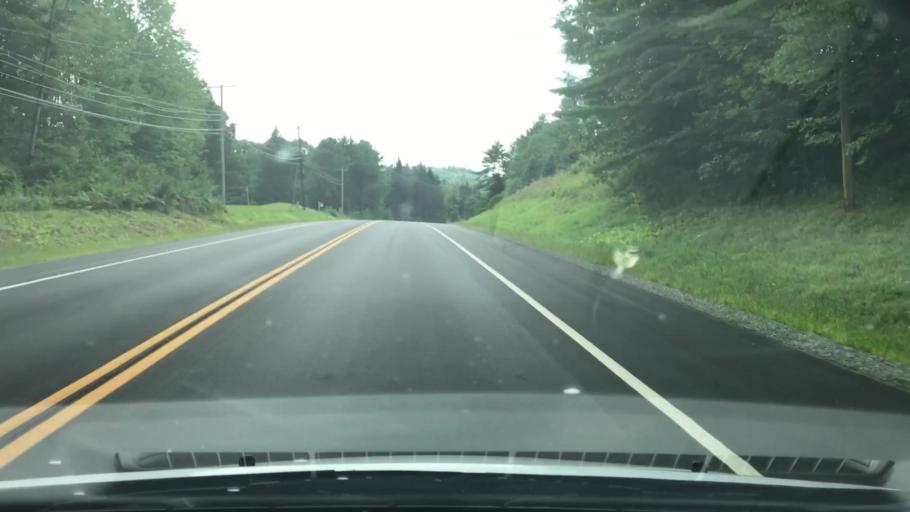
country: US
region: New Hampshire
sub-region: Grafton County
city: Lyme
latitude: 43.7552
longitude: -72.2076
